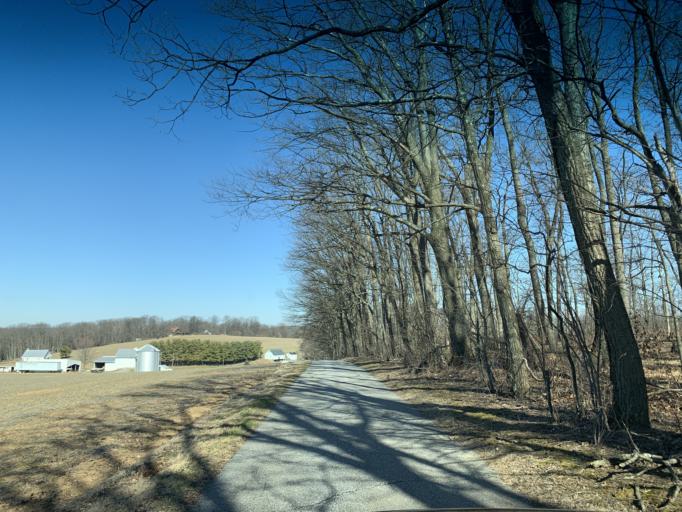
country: US
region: Maryland
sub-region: Carroll County
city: Manchester
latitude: 39.6324
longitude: -76.9189
